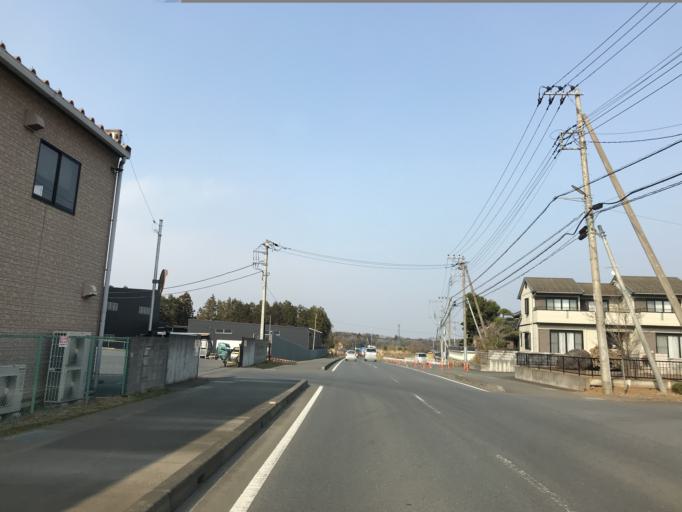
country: JP
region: Ibaraki
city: Okunoya
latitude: 36.2134
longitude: 140.4061
